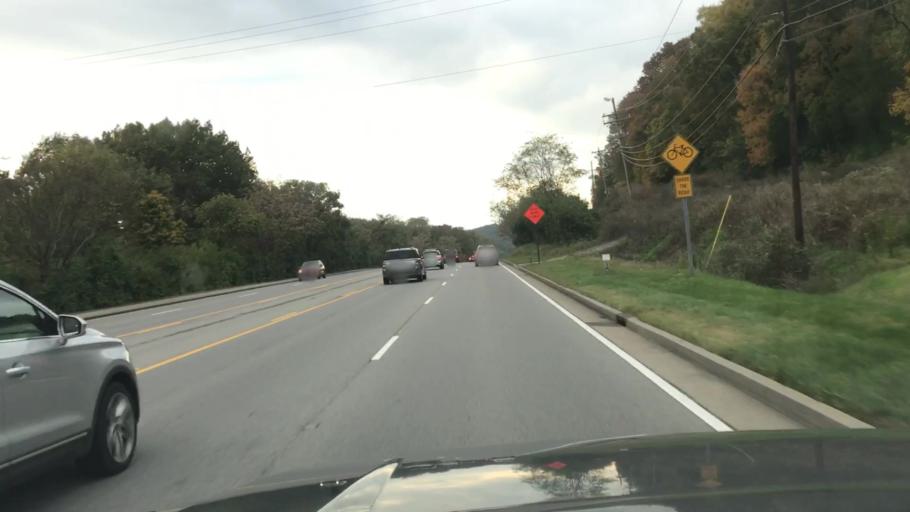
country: US
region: Tennessee
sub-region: Williamson County
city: Franklin
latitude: 35.9708
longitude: -86.8225
